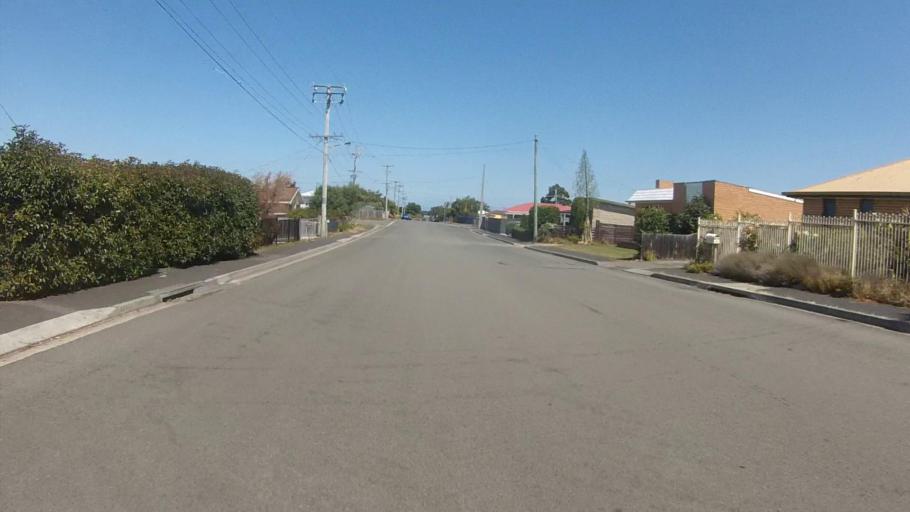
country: AU
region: Tasmania
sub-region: Sorell
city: Sorell
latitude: -42.8007
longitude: 147.5342
